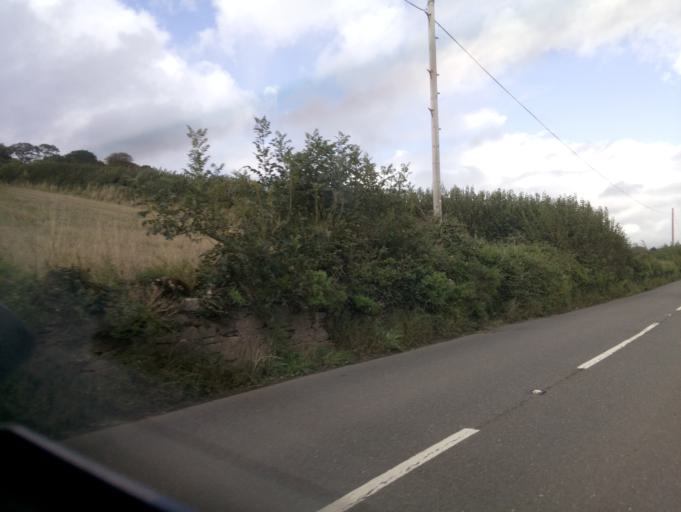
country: GB
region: England
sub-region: Devon
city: Modbury
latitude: 50.3496
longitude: -3.9173
